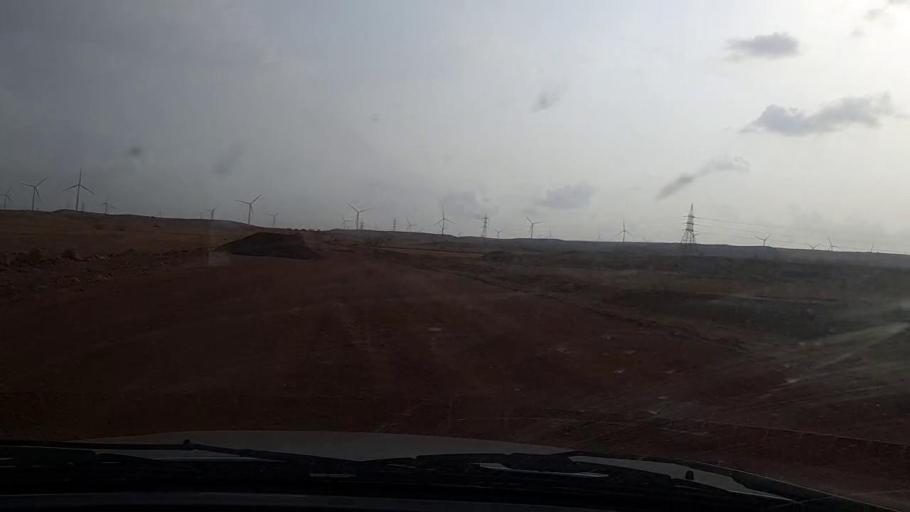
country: PK
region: Sindh
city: Thatta
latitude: 25.0571
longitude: 67.8807
